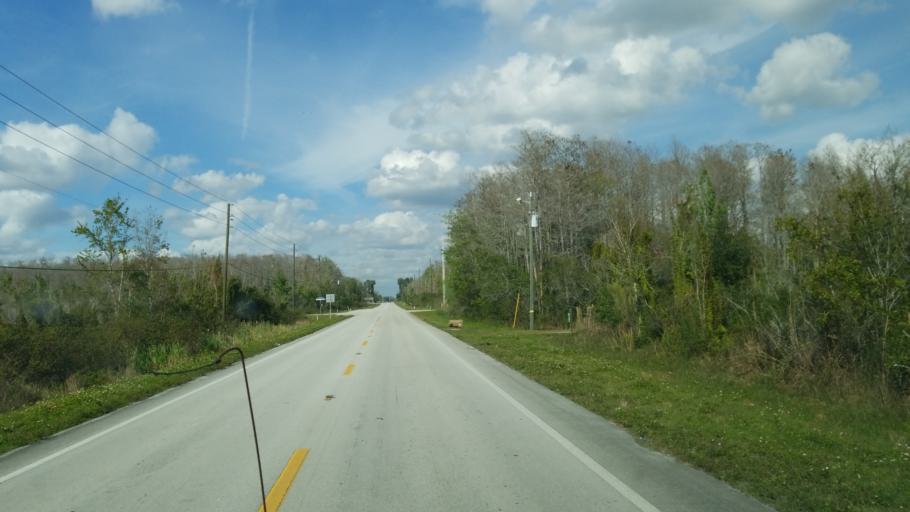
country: US
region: Florida
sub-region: Osceola County
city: Saint Cloud
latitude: 28.1299
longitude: -81.0763
